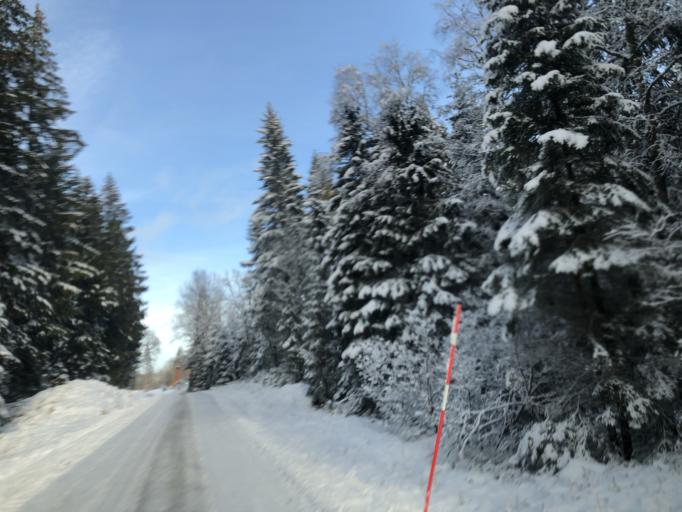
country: SE
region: Vaestra Goetaland
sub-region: Ulricehamns Kommun
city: Ulricehamn
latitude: 57.7514
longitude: 13.5100
